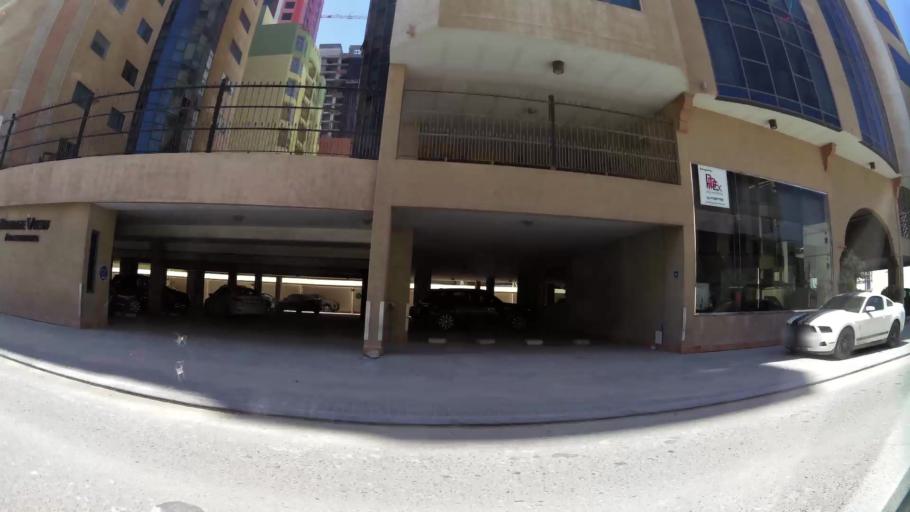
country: BH
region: Manama
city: Manama
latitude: 26.2166
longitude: 50.6123
